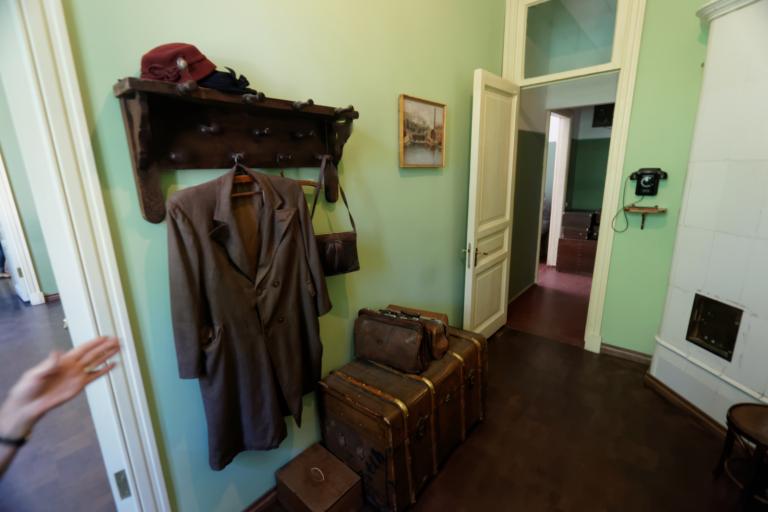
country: RU
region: St.-Petersburg
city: Centralniy
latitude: 59.9359
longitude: 30.3468
